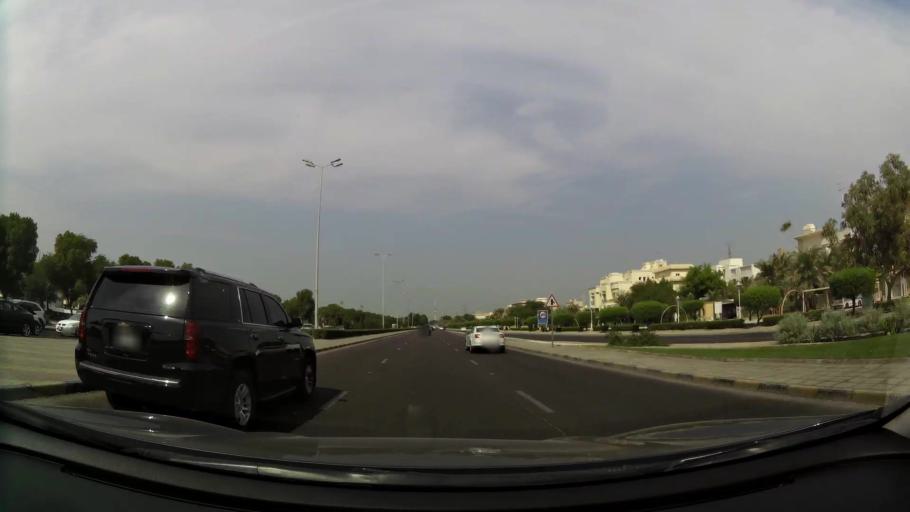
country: KW
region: Muhafazat Hawalli
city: Hawalli
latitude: 29.3216
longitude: 47.9931
